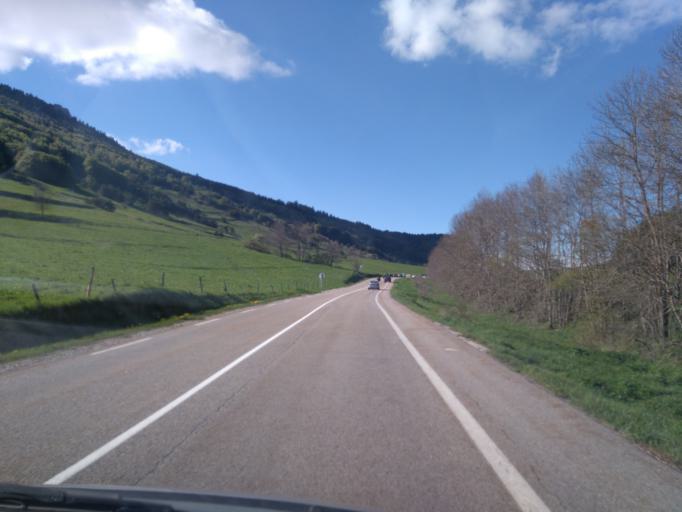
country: FR
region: Rhone-Alpes
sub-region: Departement de l'Isere
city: Mens
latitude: 44.7164
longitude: 5.6767
